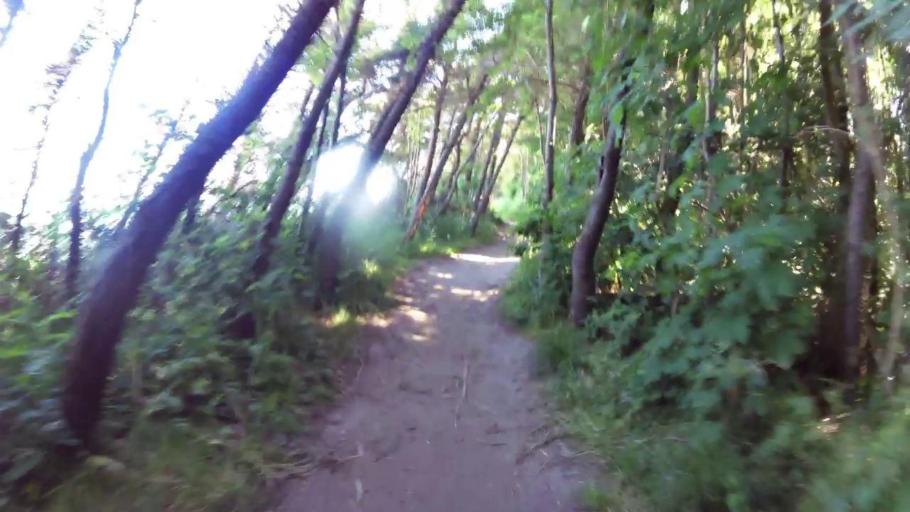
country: PL
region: West Pomeranian Voivodeship
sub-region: Powiat gryficki
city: Rewal
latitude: 54.0800
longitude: 15.0013
